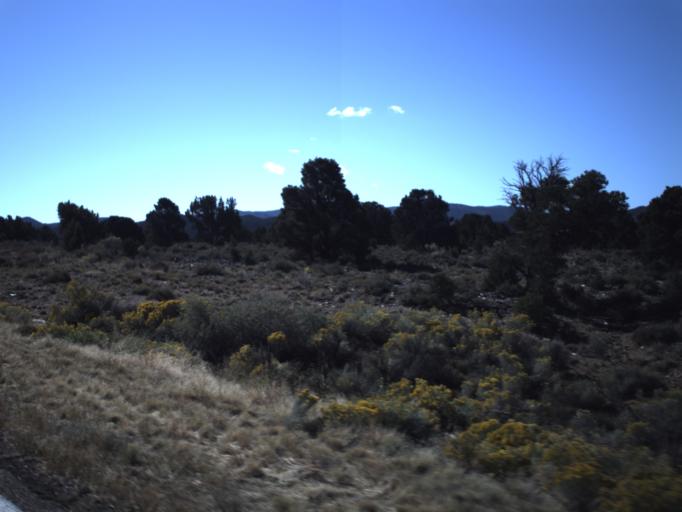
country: US
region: Utah
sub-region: Washington County
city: Enterprise
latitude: 37.6307
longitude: -113.4265
